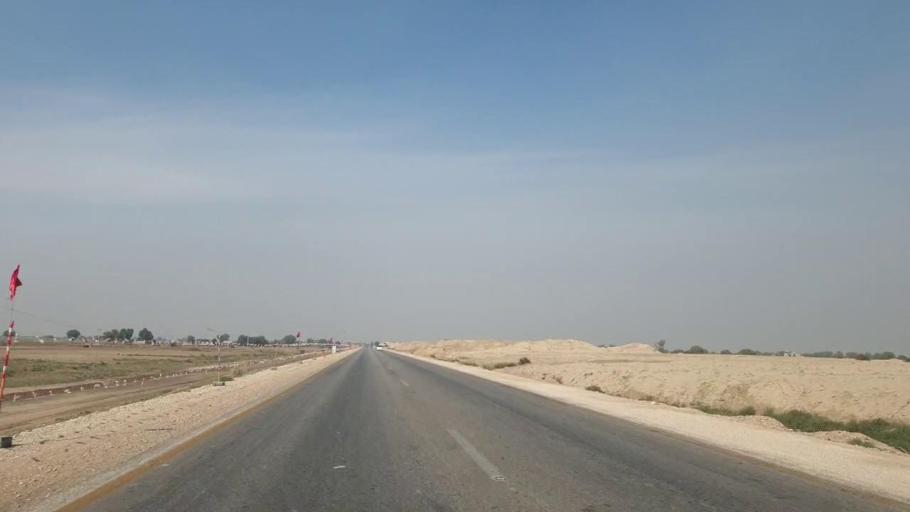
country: PK
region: Sindh
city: Sann
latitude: 25.9673
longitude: 68.1896
